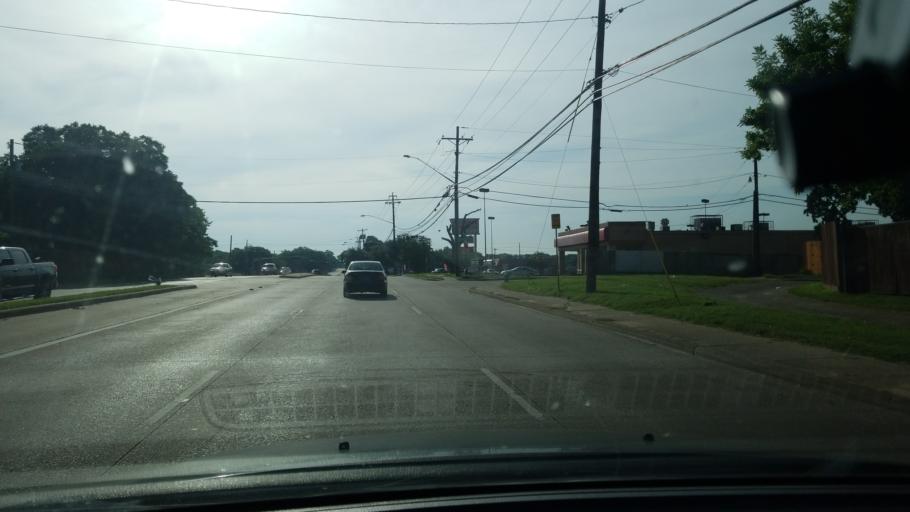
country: US
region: Texas
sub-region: Dallas County
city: Balch Springs
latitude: 32.7486
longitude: -96.6510
